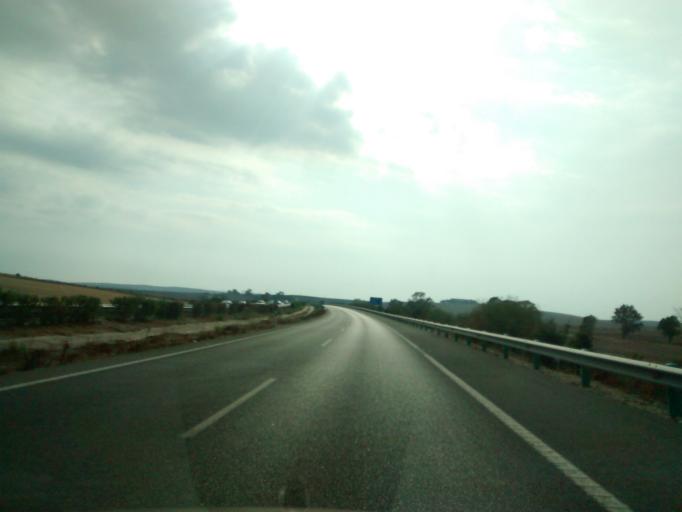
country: ES
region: Andalusia
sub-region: Provincia de Cadiz
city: Arcos de la Frontera
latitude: 36.7403
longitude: -5.8817
